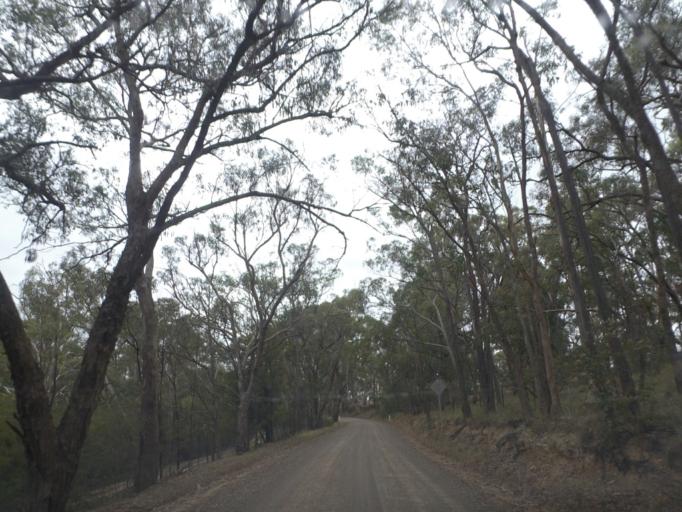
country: AU
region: Victoria
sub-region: Yarra Ranges
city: Yarra Glen
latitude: -37.6597
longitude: 145.3400
